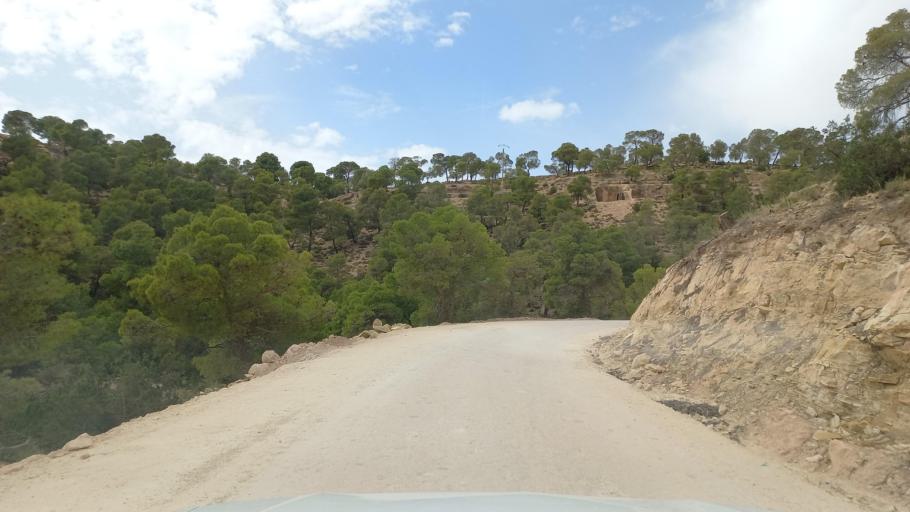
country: TN
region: Al Qasrayn
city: Kasserine
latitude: 35.3780
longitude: 8.8824
